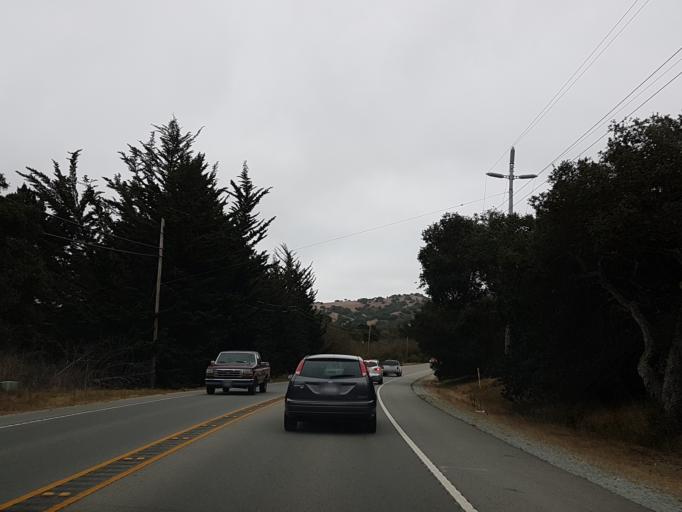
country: US
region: California
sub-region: Monterey County
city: Del Rey Oaks
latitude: 36.5700
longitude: -121.7881
